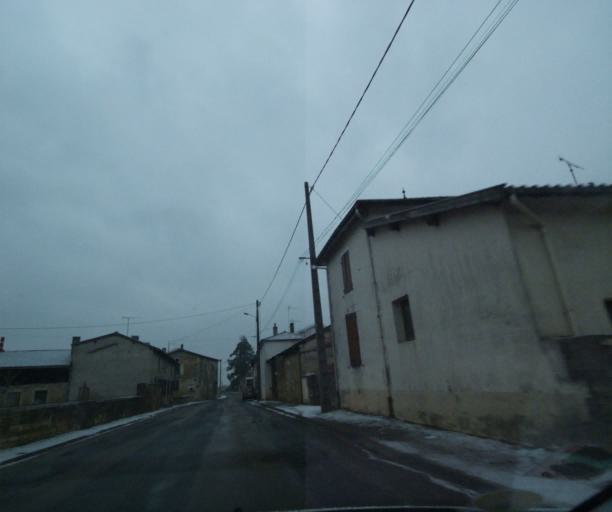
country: FR
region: Champagne-Ardenne
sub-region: Departement de la Haute-Marne
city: Wassy
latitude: 48.4316
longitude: 5.0046
